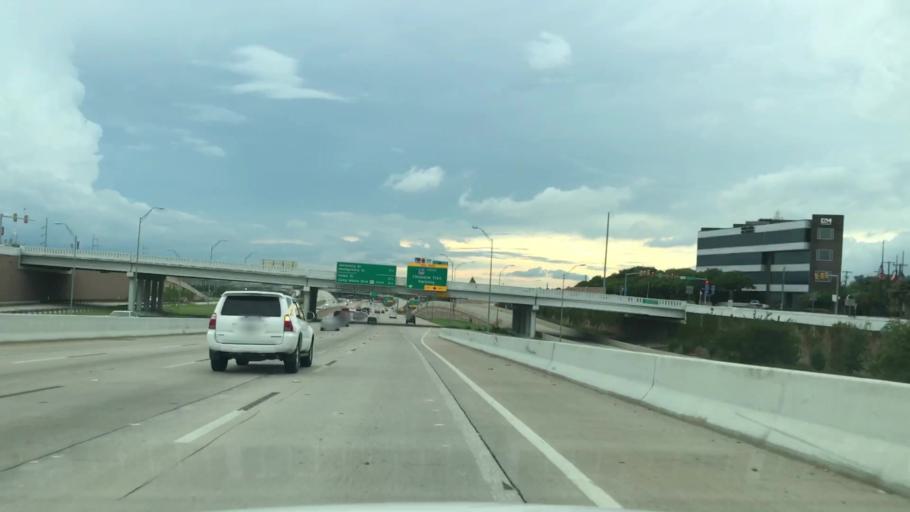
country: US
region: Texas
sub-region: Tarrant County
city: Fort Worth
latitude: 32.7429
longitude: -97.3404
